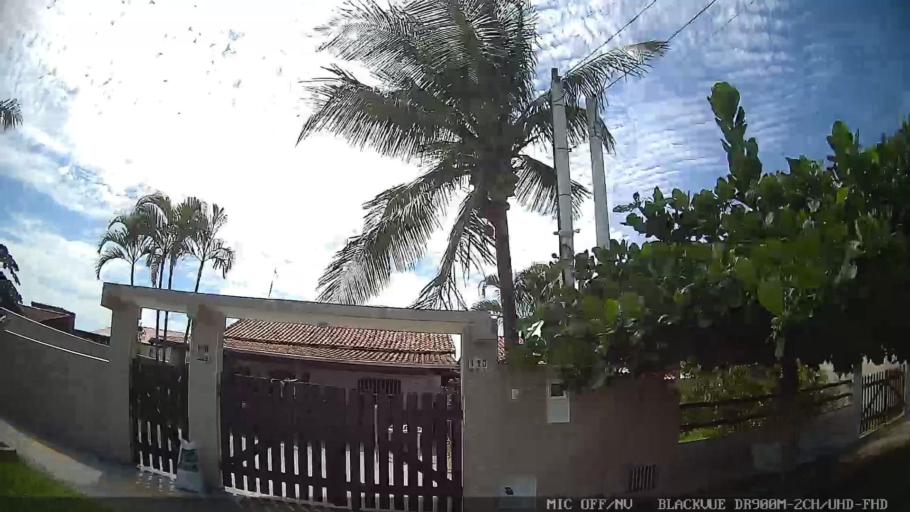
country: BR
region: Sao Paulo
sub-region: Iguape
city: Iguape
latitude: -24.7933
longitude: -47.6213
